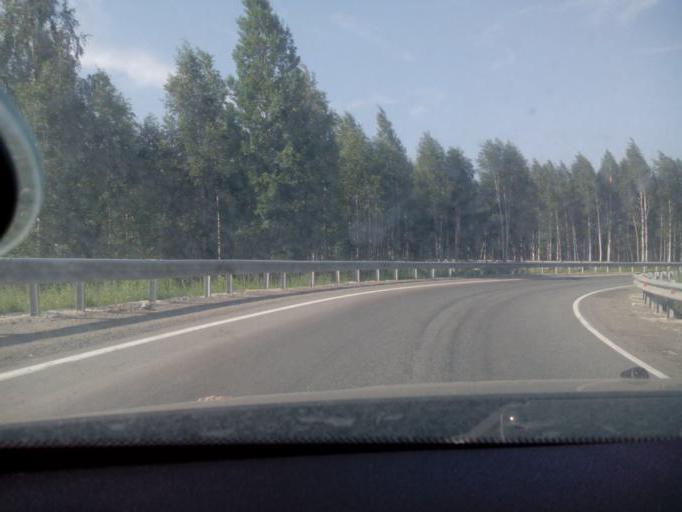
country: RU
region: Sverdlovsk
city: Verkh-Neyvinskiy
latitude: 57.3077
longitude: 60.2912
